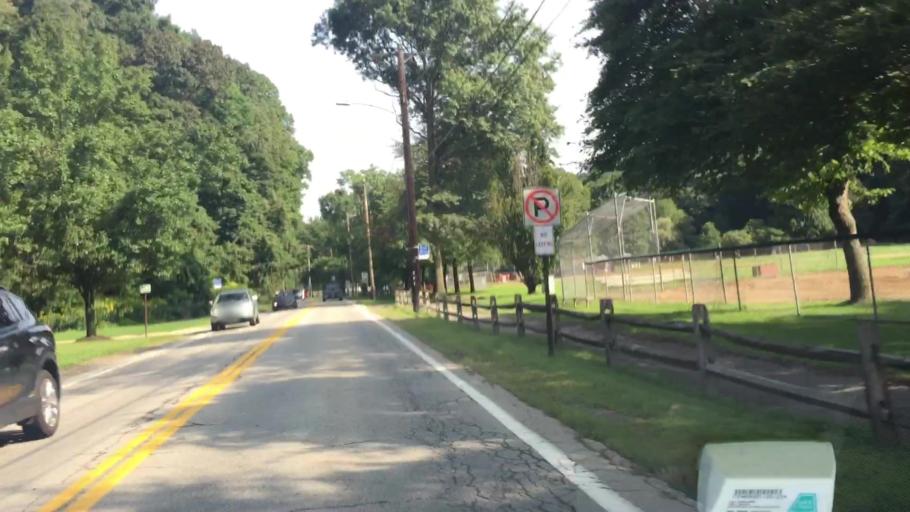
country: US
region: Pennsylvania
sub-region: Allegheny County
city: Fox Chapel
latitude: 40.4955
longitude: -79.8821
